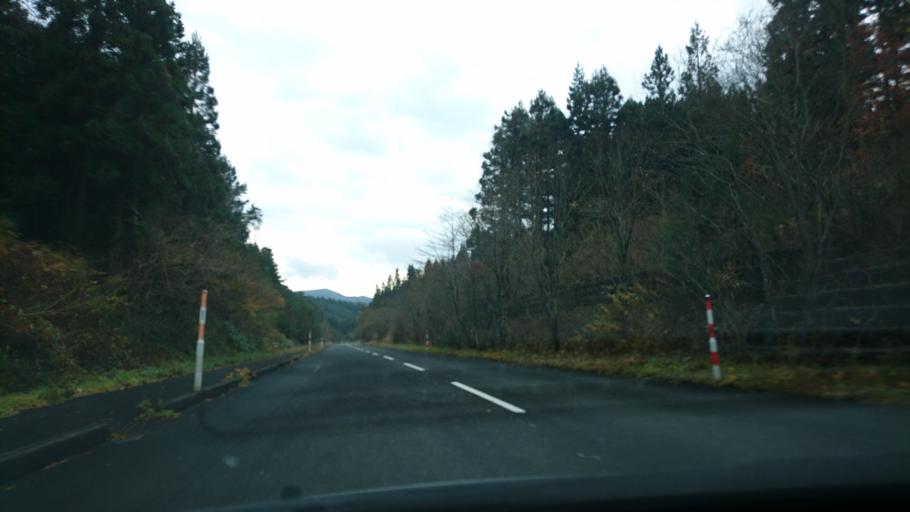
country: JP
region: Iwate
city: Ichinoseki
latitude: 38.9236
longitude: 140.9090
